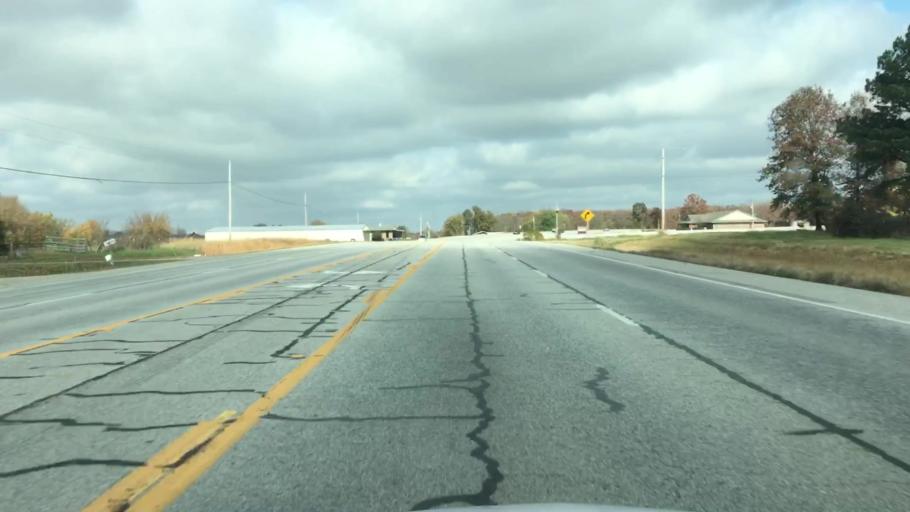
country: US
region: Arkansas
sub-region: Benton County
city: Gentry
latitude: 36.2274
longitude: -94.4951
